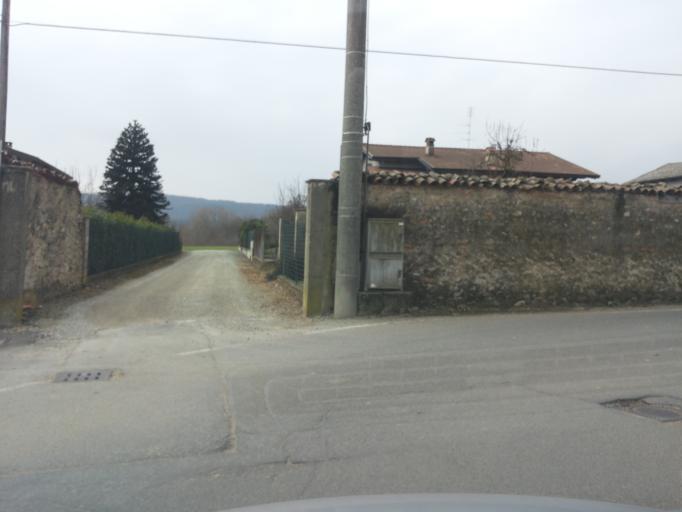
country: IT
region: Piedmont
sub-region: Provincia di Biella
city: Vergnasco
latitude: 45.4725
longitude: 8.0874
